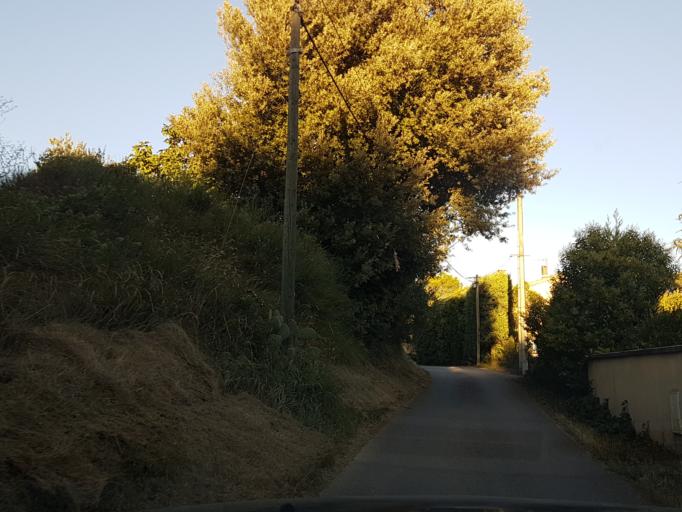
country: FR
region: Provence-Alpes-Cote d'Azur
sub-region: Departement du Vaucluse
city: Pernes-les-Fontaines
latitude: 43.9853
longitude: 5.0669
